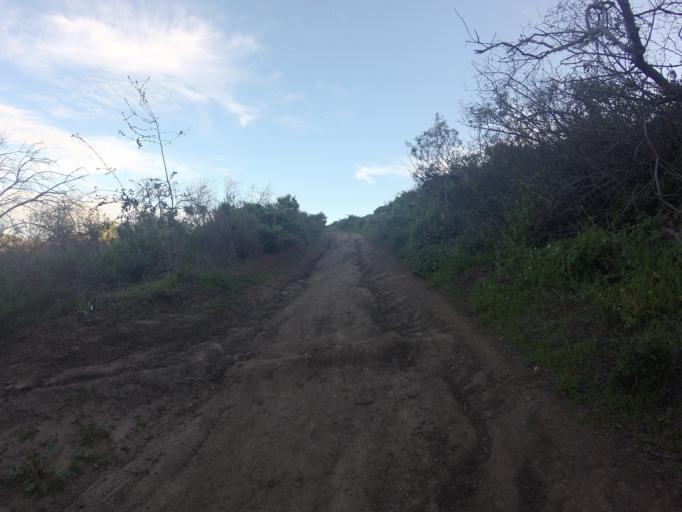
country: US
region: California
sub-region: Orange County
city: Laguna Beach
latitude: 33.5907
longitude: -117.7765
